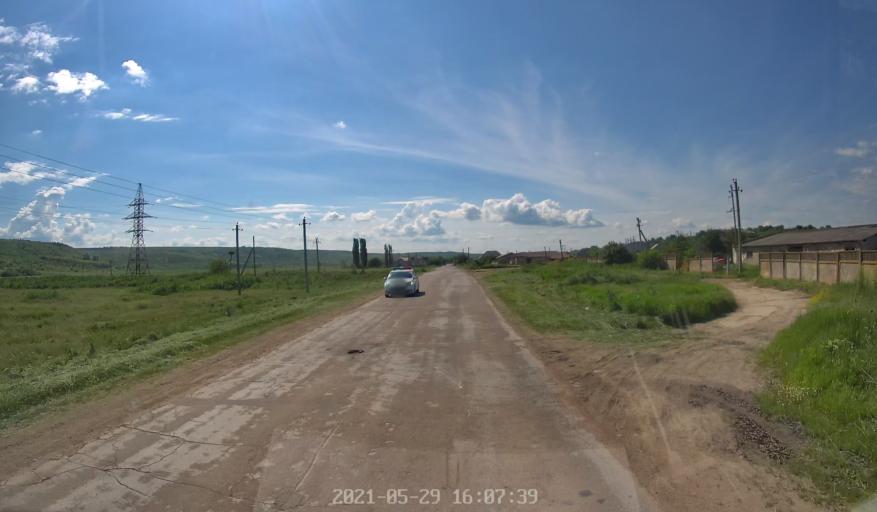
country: MD
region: Chisinau
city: Singera
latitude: 46.8168
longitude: 28.8988
